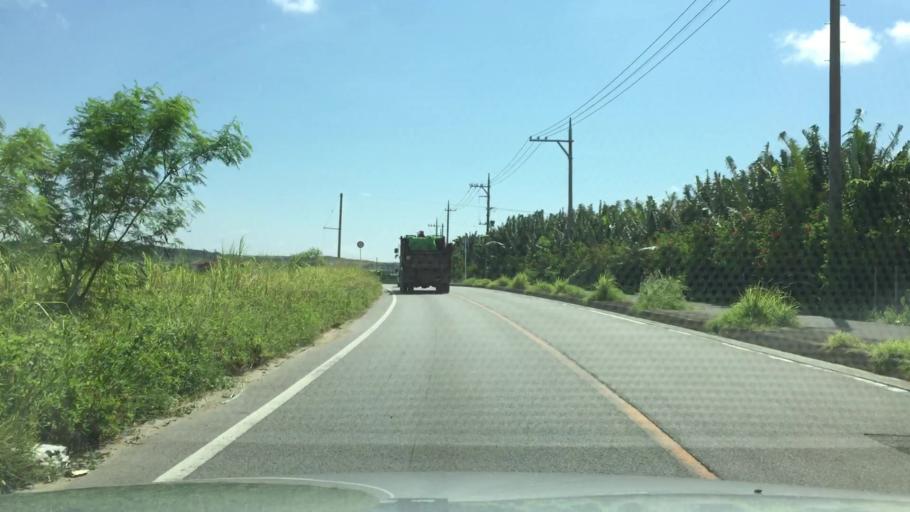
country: JP
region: Okinawa
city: Ishigaki
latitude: 24.3557
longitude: 124.1949
